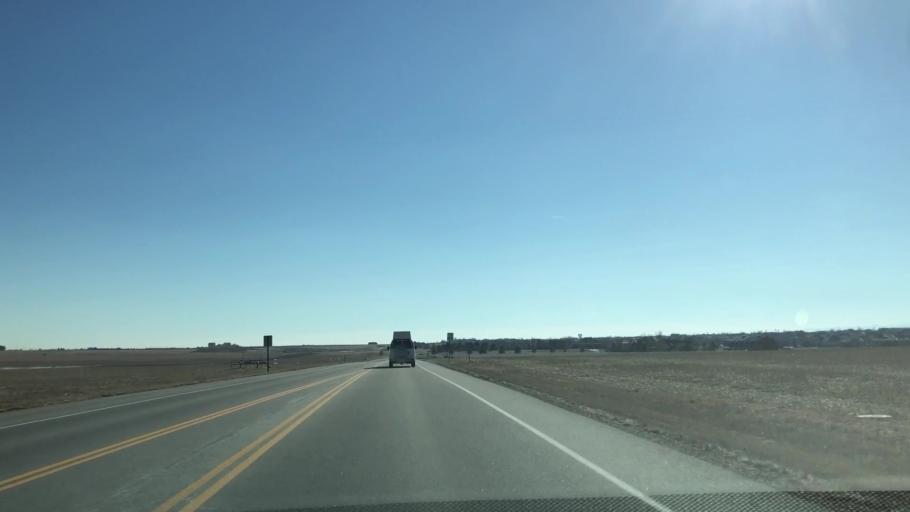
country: US
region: Colorado
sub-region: Weld County
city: Windsor
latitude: 40.4605
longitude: -104.9442
